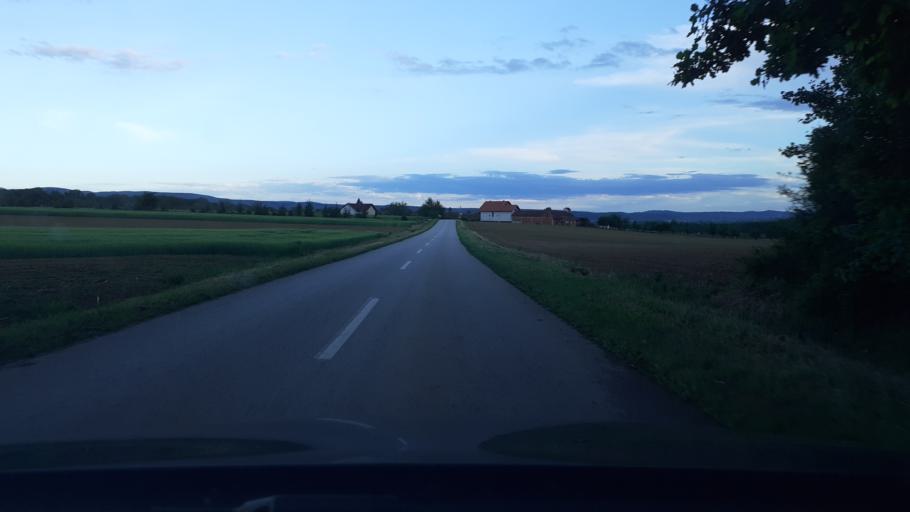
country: HR
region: Pozesko-Slavonska
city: Jaksic
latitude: 45.3427
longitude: 17.7913
